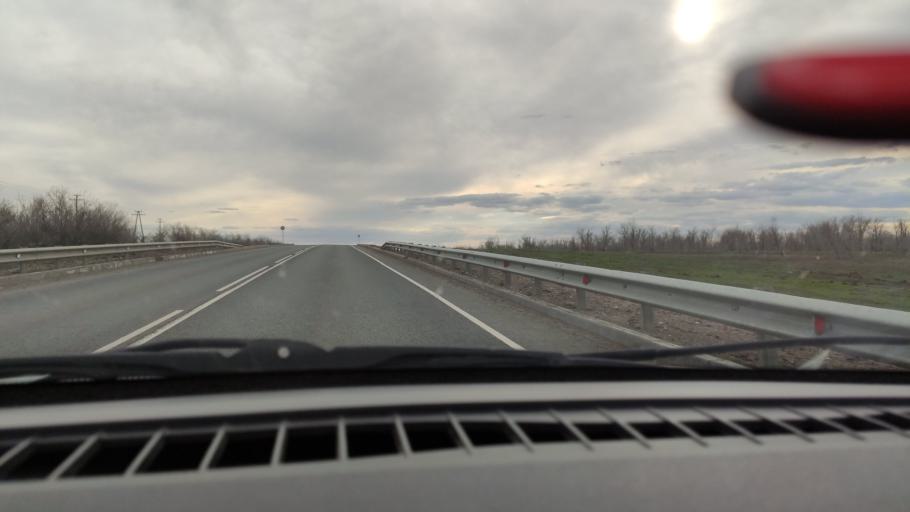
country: RU
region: Bashkortostan
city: Mayachnyy
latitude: 52.3424
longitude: 55.5364
